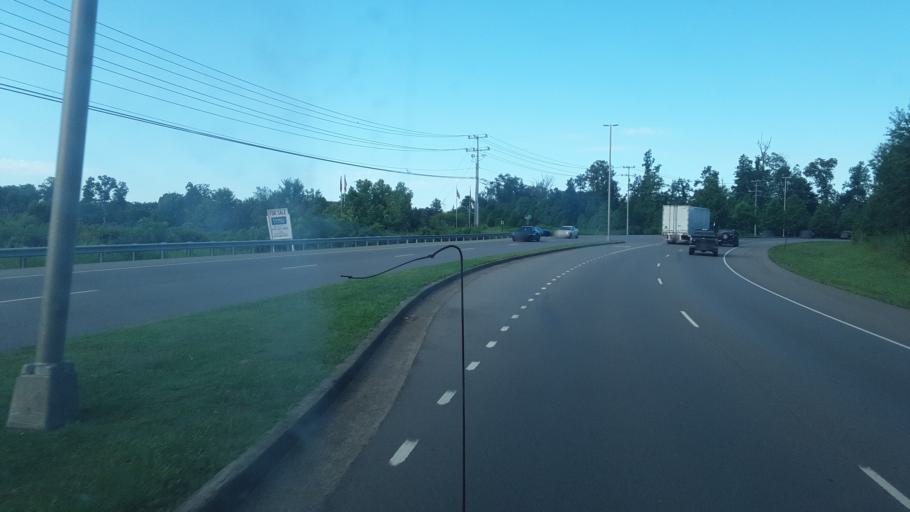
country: US
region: Tennessee
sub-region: Montgomery County
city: Clarksville
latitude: 36.5786
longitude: -87.2783
